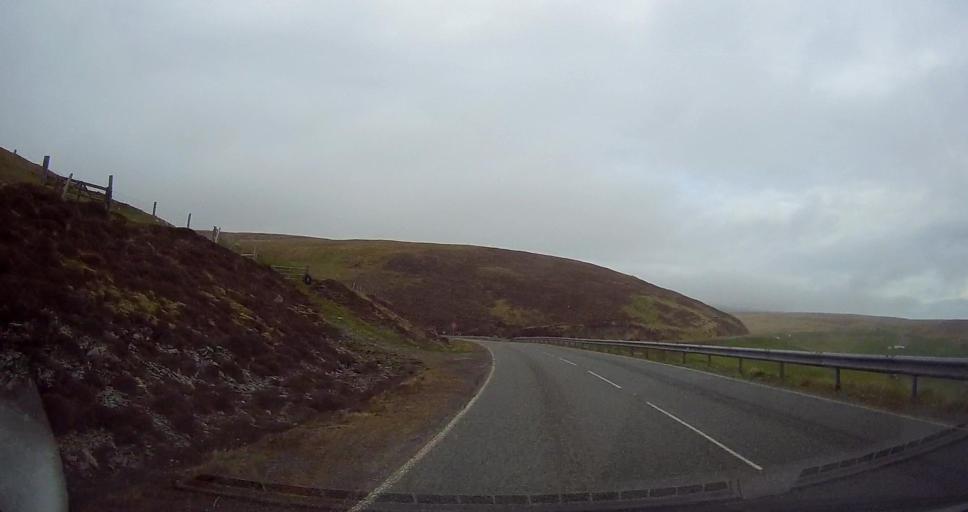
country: GB
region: Scotland
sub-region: Shetland Islands
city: Sandwick
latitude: 59.9885
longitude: -1.2838
